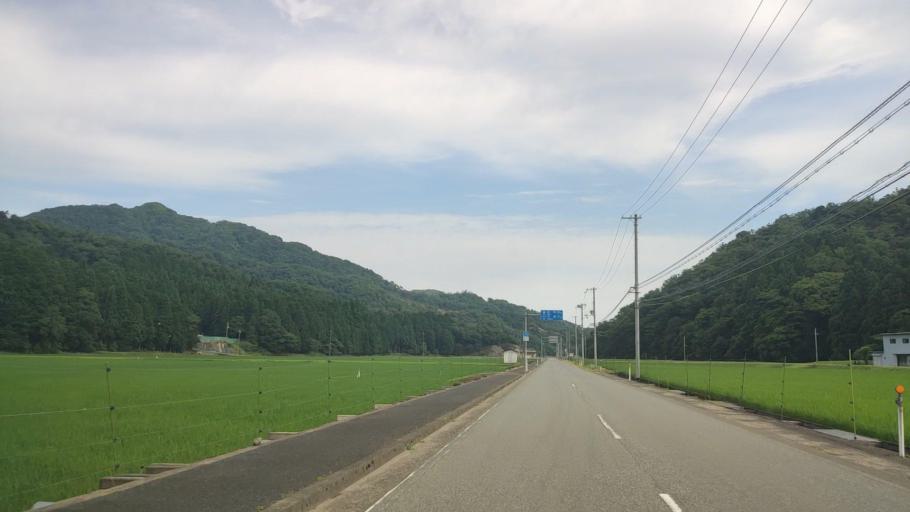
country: JP
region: Hyogo
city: Toyooka
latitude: 35.6153
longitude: 134.8440
